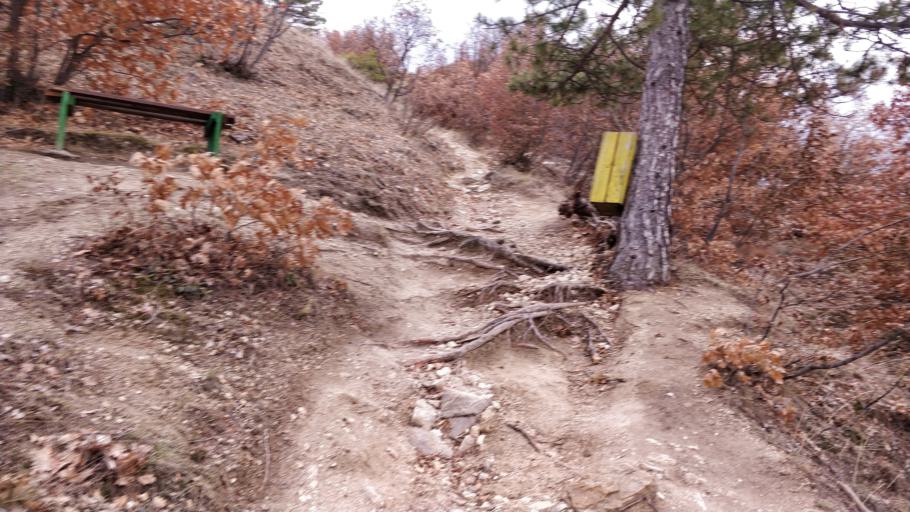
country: BG
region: Kyustendil
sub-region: Obshtina Rila
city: Rila
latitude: 42.0940
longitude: 23.1158
